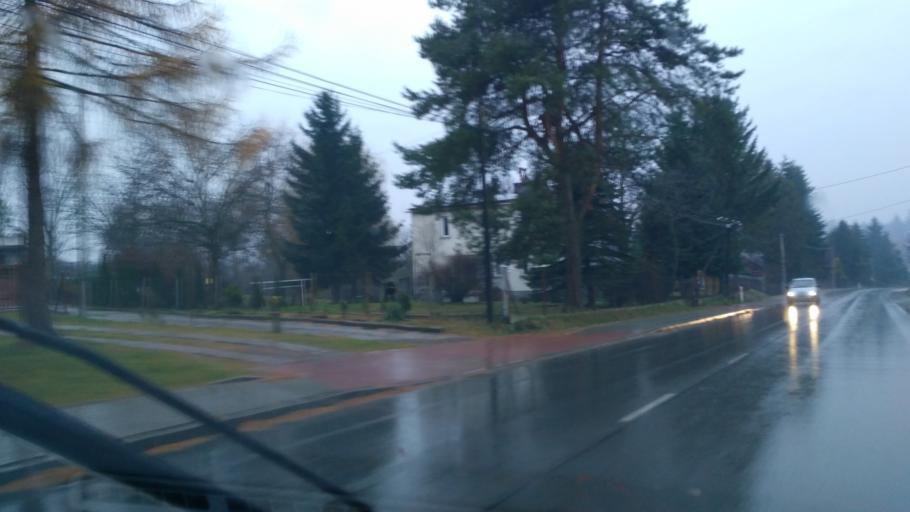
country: PL
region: Subcarpathian Voivodeship
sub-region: Powiat lancucki
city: Krzemienica
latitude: 50.0719
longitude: 22.1967
